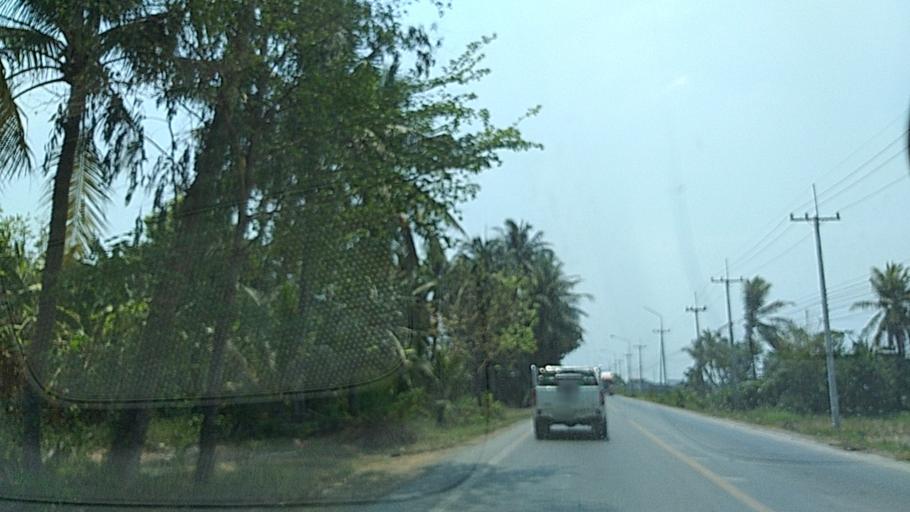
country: TH
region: Chachoengsao
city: Bang Nam Priao
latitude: 13.8609
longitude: 100.9662
